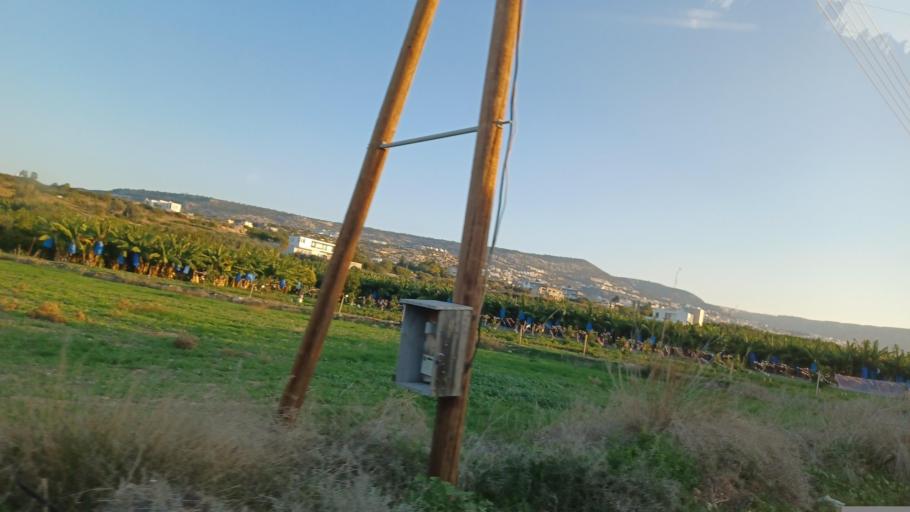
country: CY
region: Pafos
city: Pegeia
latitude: 34.8682
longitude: 32.3571
